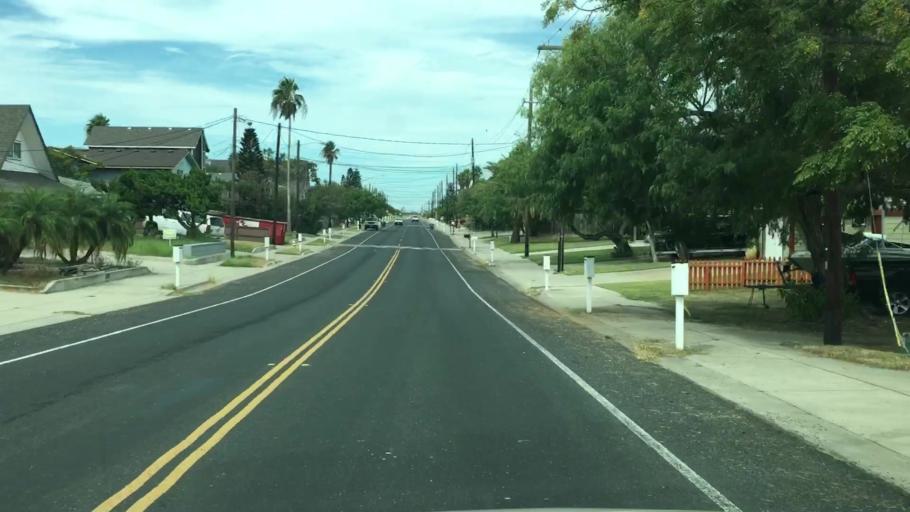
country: US
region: Texas
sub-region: Nueces County
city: Corpus Christi
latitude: 27.6281
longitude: -97.2923
